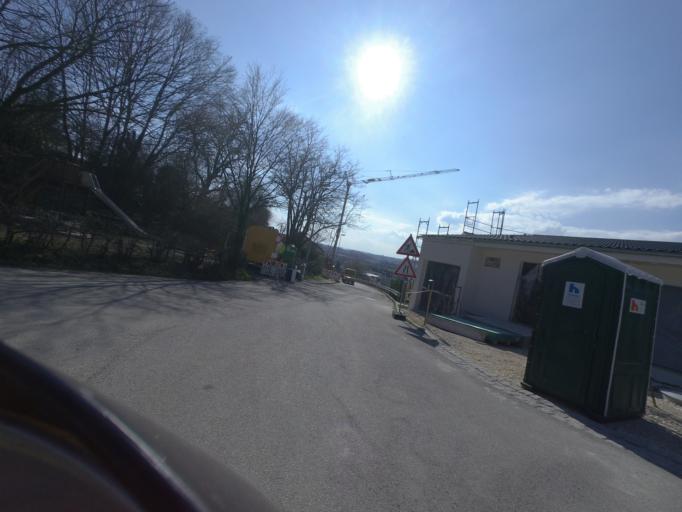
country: DE
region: Baden-Wuerttemberg
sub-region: Regierungsbezirk Stuttgart
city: Oberboihingen
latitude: 48.6541
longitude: 9.3699
